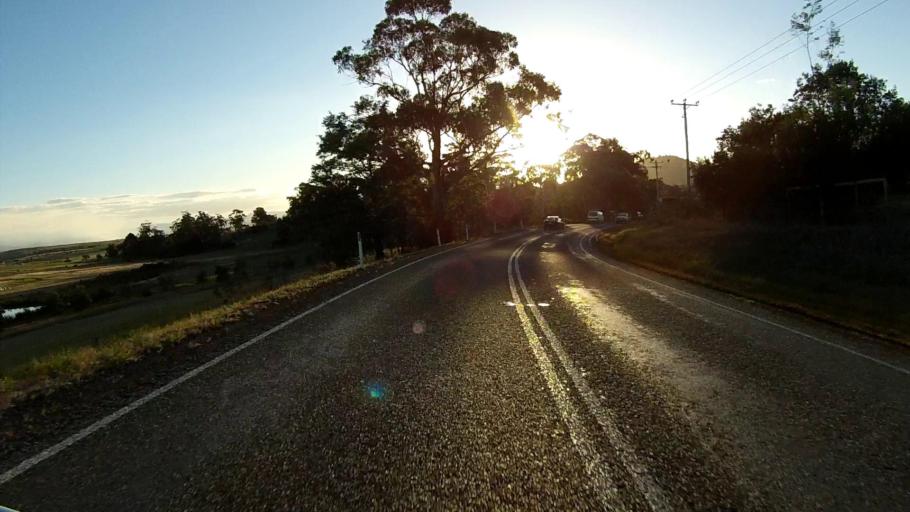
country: AU
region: Tasmania
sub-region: Sorell
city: Sorell
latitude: -42.8092
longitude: 147.6367
